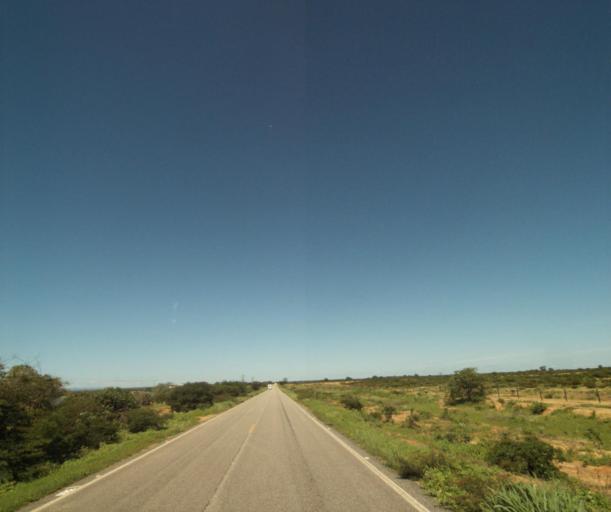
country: BR
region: Bahia
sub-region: Palmas De Monte Alto
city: Palmas de Monte Alto
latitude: -14.2565
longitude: -43.2489
